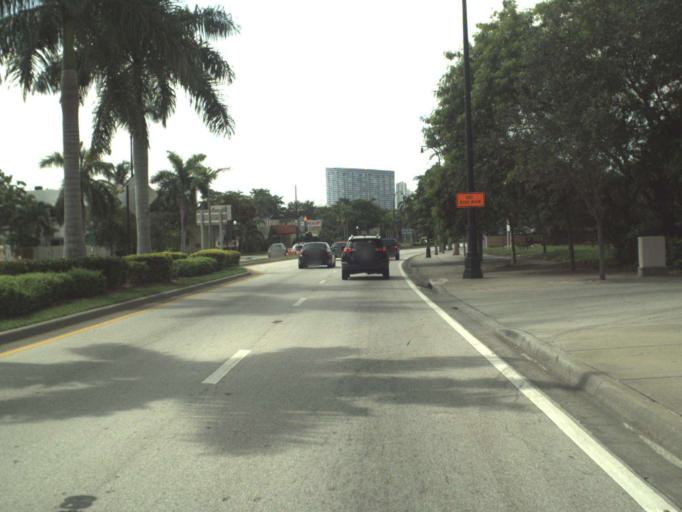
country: US
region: Florida
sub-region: Miami-Dade County
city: El Portal
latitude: 25.8248
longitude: -80.1870
